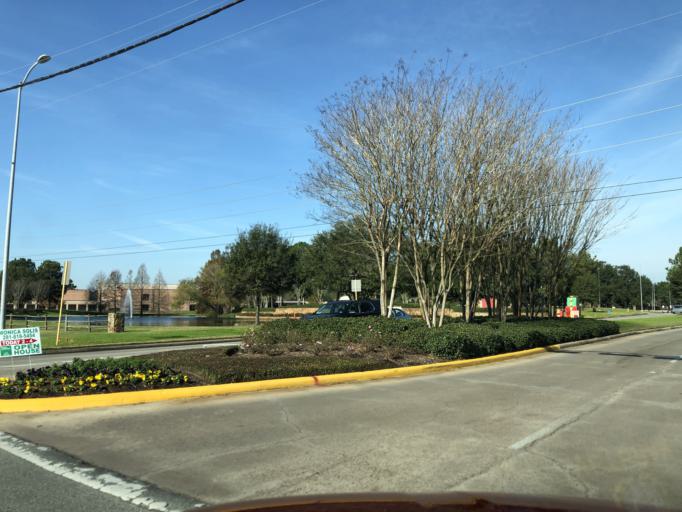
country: US
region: Texas
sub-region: Harris County
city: Tomball
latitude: 30.0272
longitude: -95.5631
